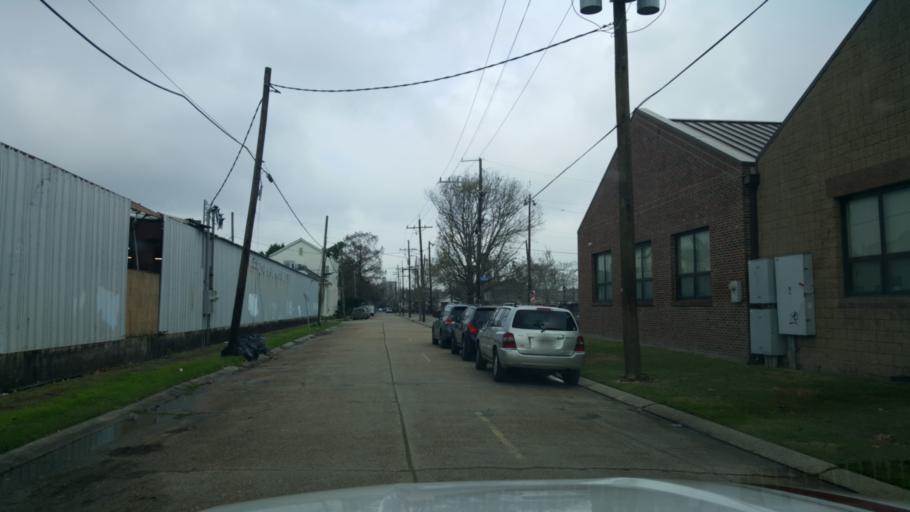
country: US
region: Louisiana
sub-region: Jefferson Parish
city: Gretna
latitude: 29.9325
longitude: -90.0684
